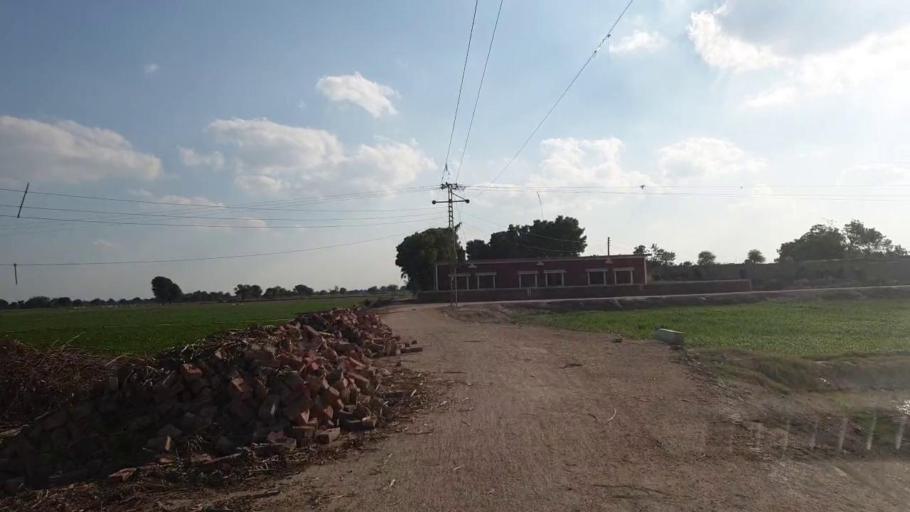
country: PK
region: Sindh
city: Shahpur Chakar
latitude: 26.1024
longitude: 68.5825
